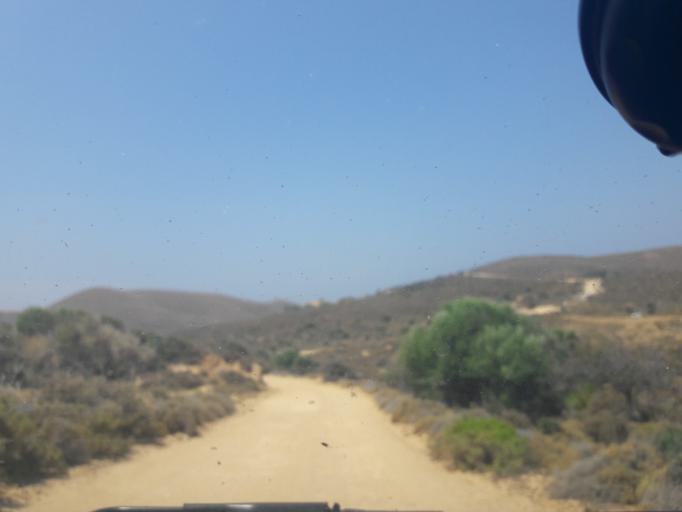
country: GR
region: North Aegean
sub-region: Nomos Lesvou
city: Myrina
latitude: 39.9888
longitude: 25.1356
